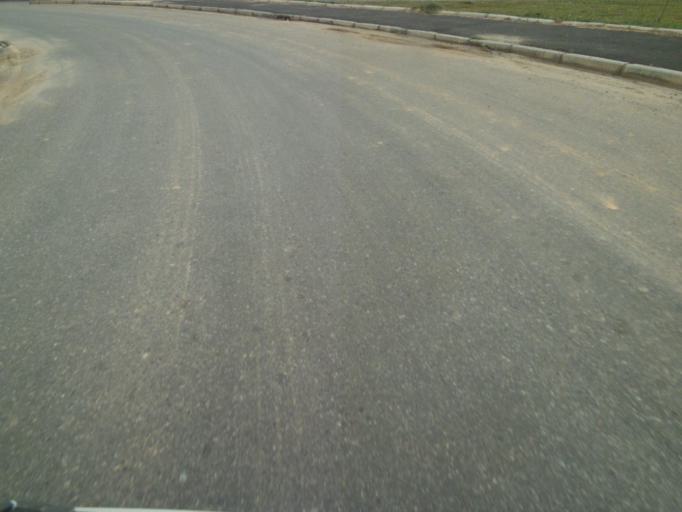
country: BR
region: Parana
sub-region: Palmeira
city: Palmeira
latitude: -25.4372
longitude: -50.0124
